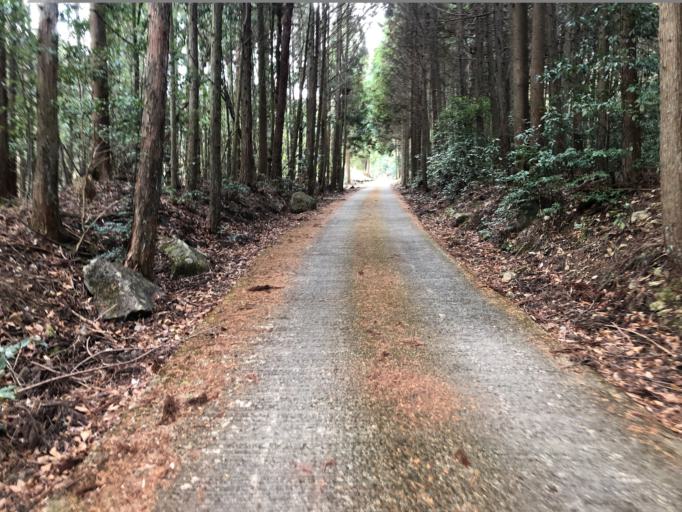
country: JP
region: Kyoto
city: Kameoka
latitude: 35.0350
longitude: 135.4750
